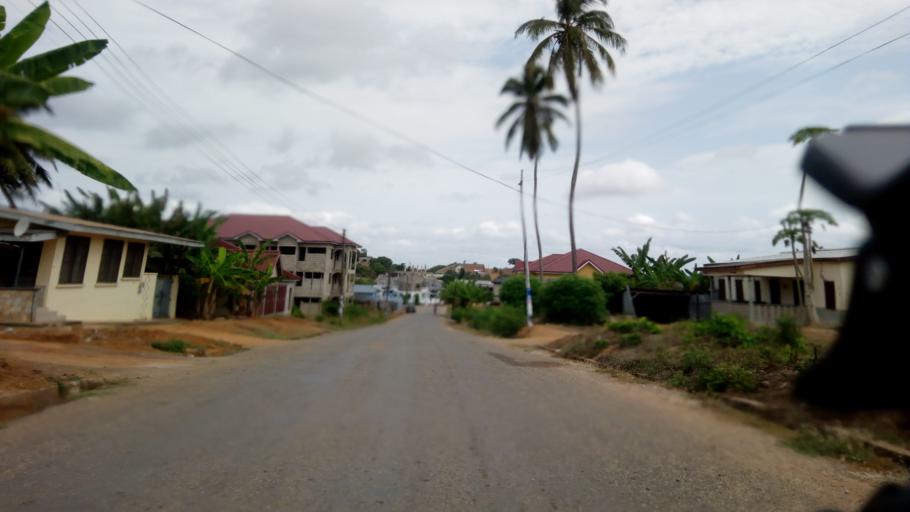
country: GH
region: Central
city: Cape Coast
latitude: 5.1060
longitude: -1.2713
